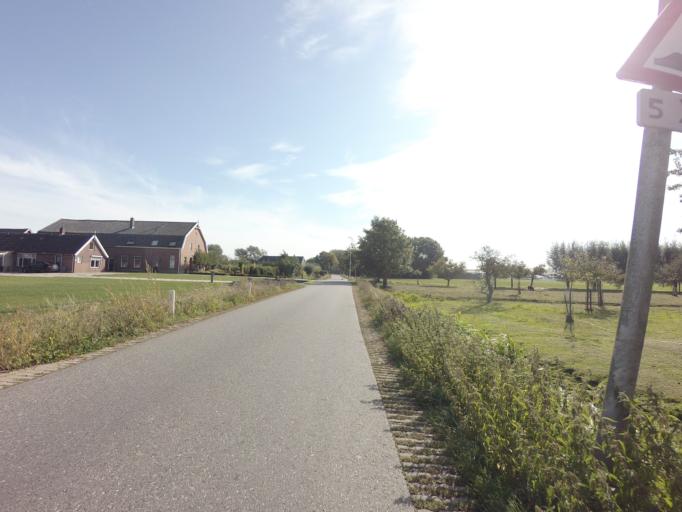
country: NL
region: South Holland
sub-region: Gemeente Leerdam
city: Leerdam
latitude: 51.9176
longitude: 5.0709
